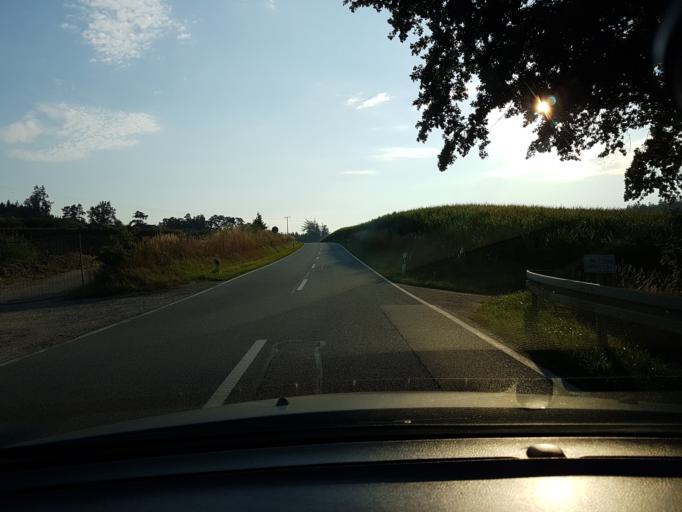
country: DE
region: Bavaria
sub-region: Lower Bavaria
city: Vilsbiburg
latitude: 48.4896
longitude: 12.3140
